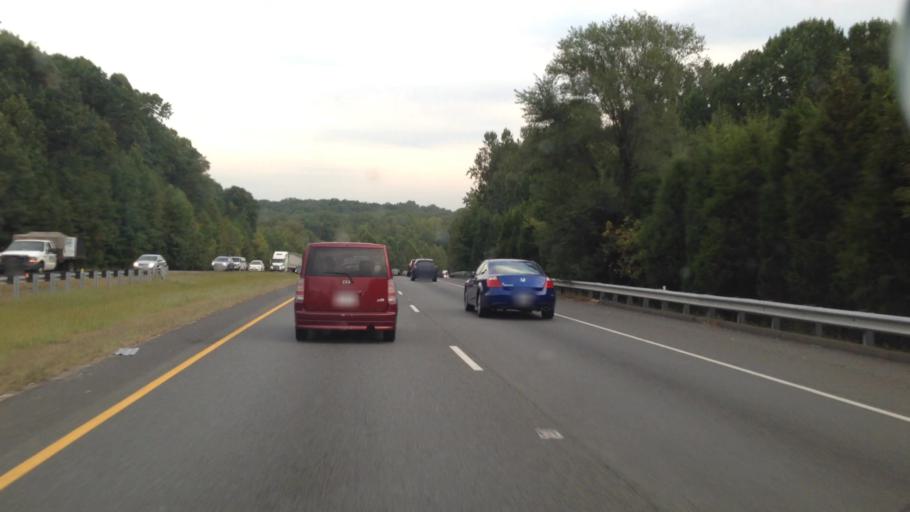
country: US
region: Virginia
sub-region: Fairfax County
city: Fairfax Station
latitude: 38.7998
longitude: -77.3405
